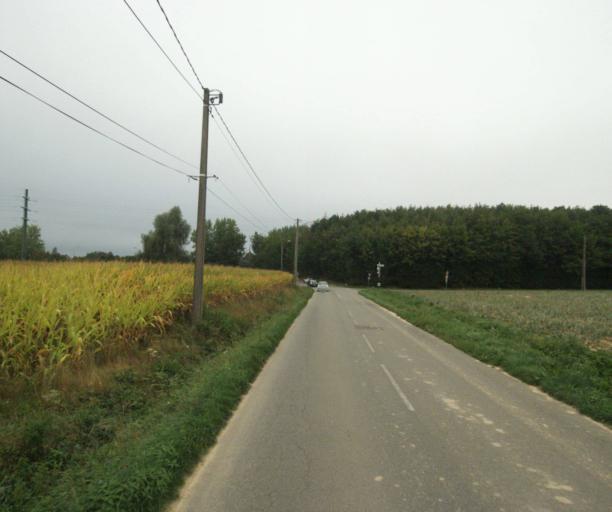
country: FR
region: Nord-Pas-de-Calais
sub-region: Departement du Nord
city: Sailly-lez-Lannoy
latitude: 50.6448
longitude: 3.2028
